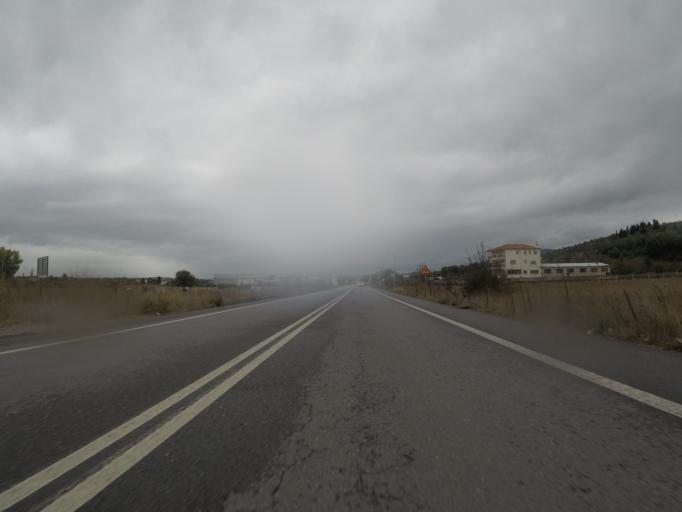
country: GR
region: Peloponnese
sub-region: Nomos Arkadias
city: Tripoli
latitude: 37.5462
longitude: 22.3948
